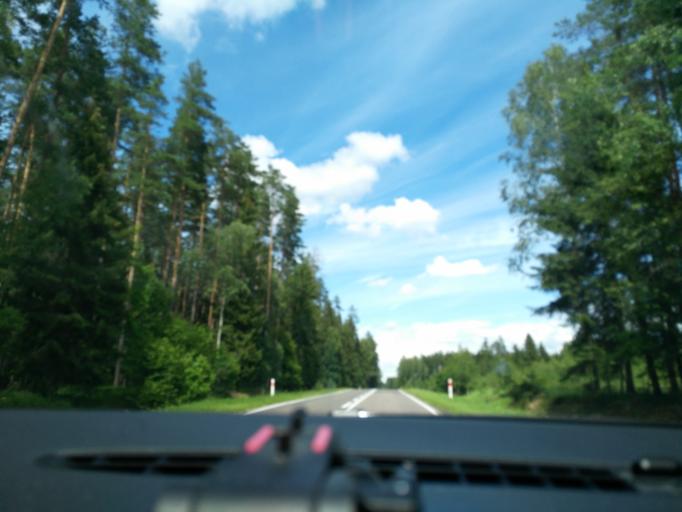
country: PL
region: Podlasie
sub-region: Powiat sejnenski
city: Sejny
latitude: 53.9925
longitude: 23.3063
